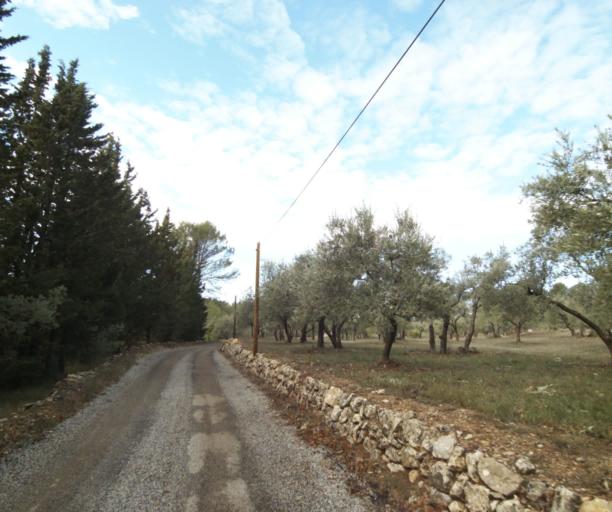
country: FR
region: Provence-Alpes-Cote d'Azur
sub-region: Departement du Var
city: Trans-en-Provence
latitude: 43.4984
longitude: 6.4656
